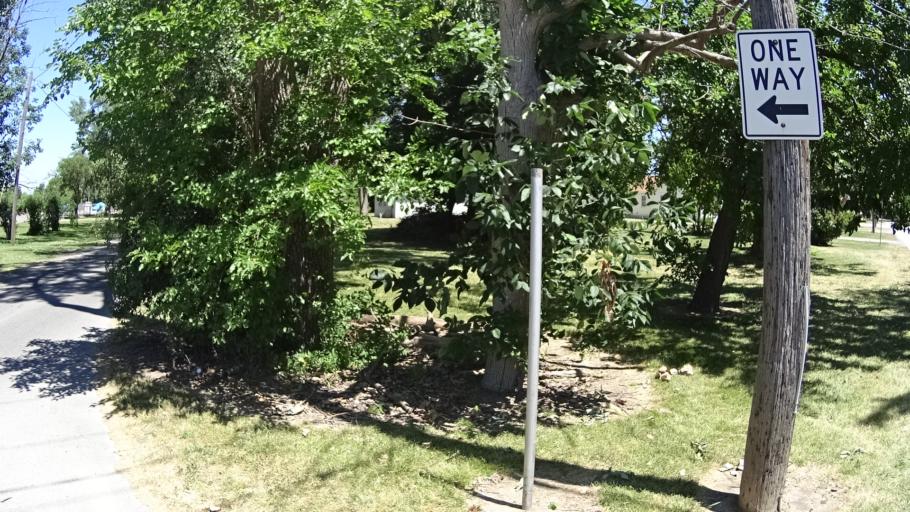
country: US
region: Ohio
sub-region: Erie County
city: Sandusky
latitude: 41.4480
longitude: -82.6729
